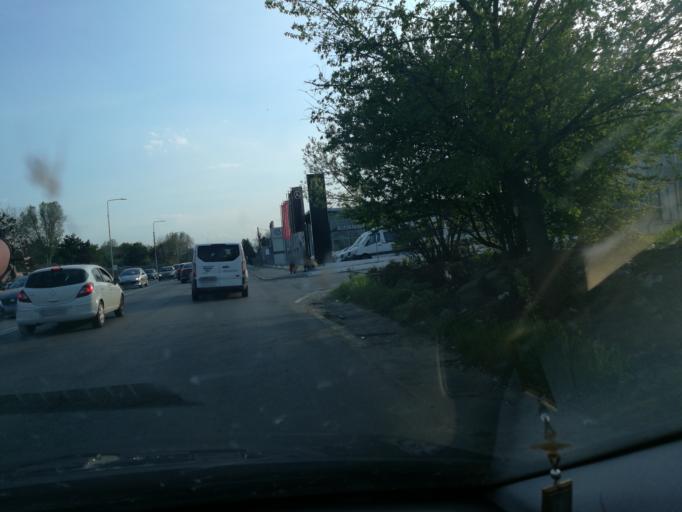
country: RO
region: Constanta
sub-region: Municipiul Constanta
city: Palazu Mare
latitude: 44.2062
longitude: 28.6134
